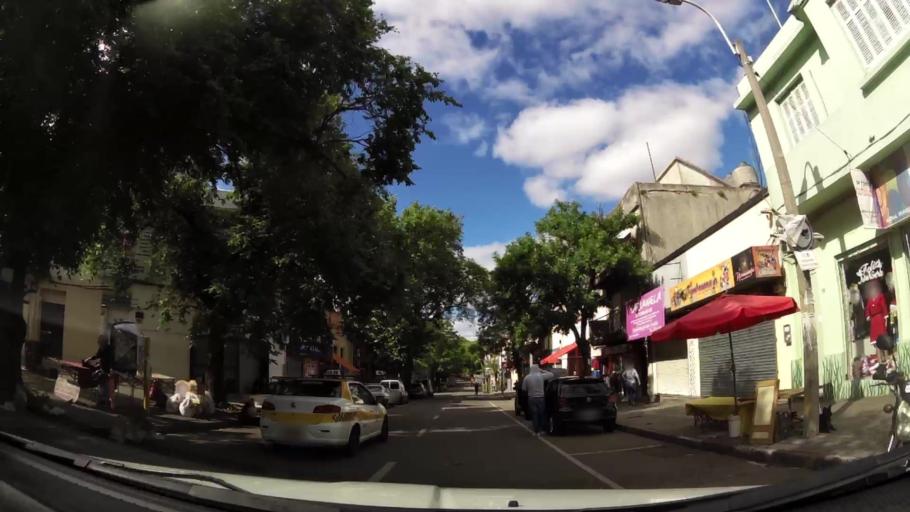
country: UY
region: Montevideo
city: Montevideo
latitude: -34.8859
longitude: -56.1798
